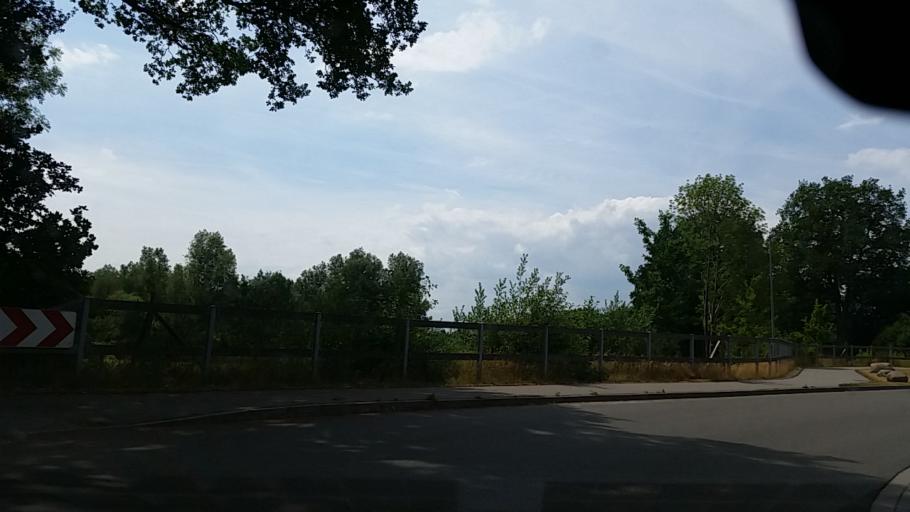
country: DE
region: Schleswig-Holstein
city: Tremsbuttel
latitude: 53.7414
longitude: 10.3146
